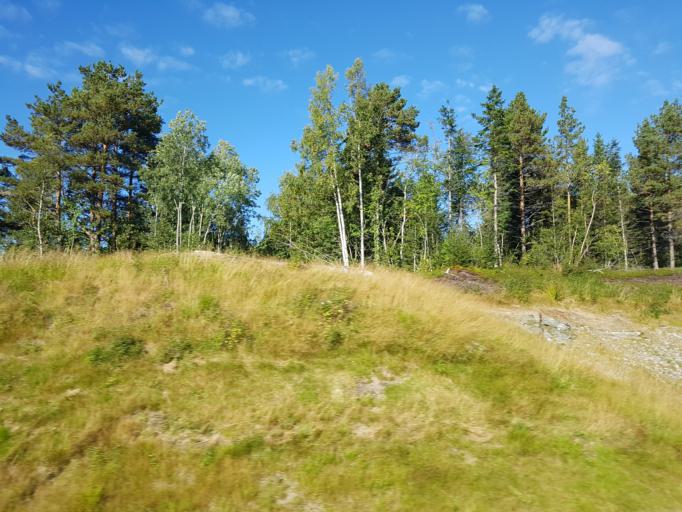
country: NO
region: Sor-Trondelag
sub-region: Trondheim
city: Trondheim
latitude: 63.5988
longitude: 10.2204
